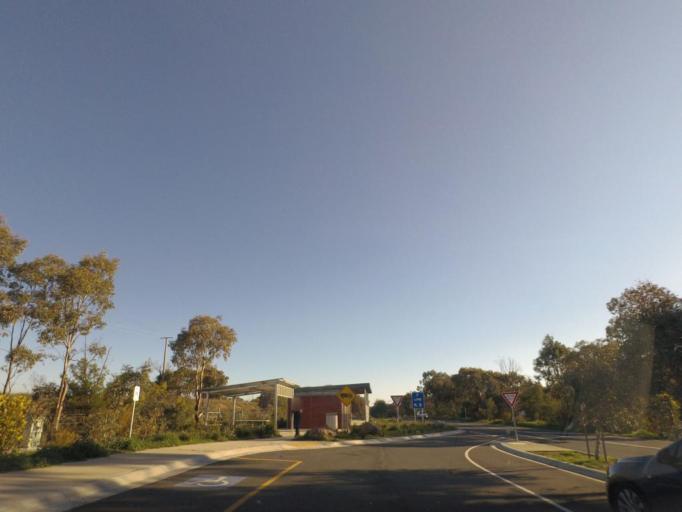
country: AU
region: Victoria
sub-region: Greater Shepparton
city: Shepparton
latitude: -36.7809
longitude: 145.5018
